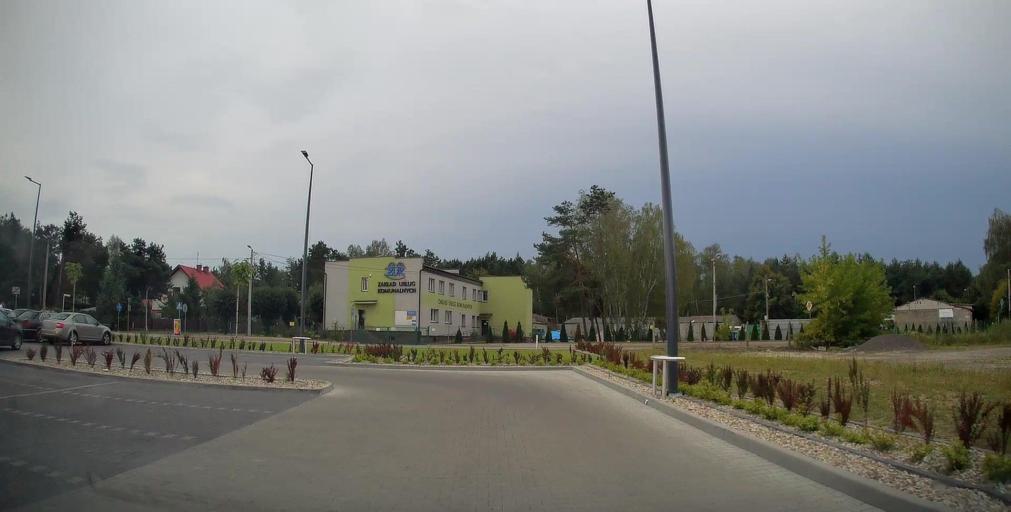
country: PL
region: Masovian Voivodeship
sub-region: Powiat bialobrzeski
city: Bialobrzegi
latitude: 51.6433
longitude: 20.9433
